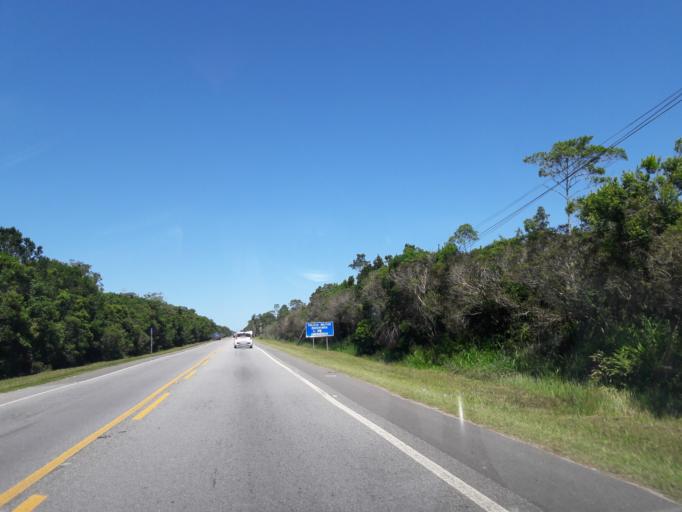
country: BR
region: Parana
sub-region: Pontal Do Parana
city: Pontal do Parana
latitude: -25.6768
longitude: -48.5059
